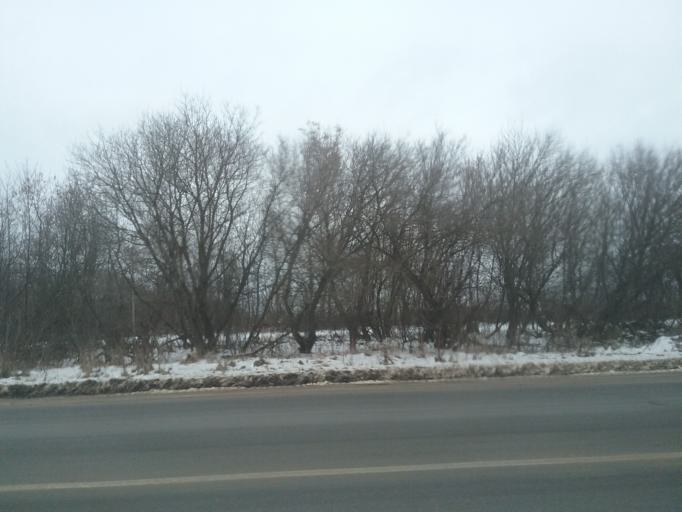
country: RU
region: Tula
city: Bolokhovo
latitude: 54.0657
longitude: 37.7989
